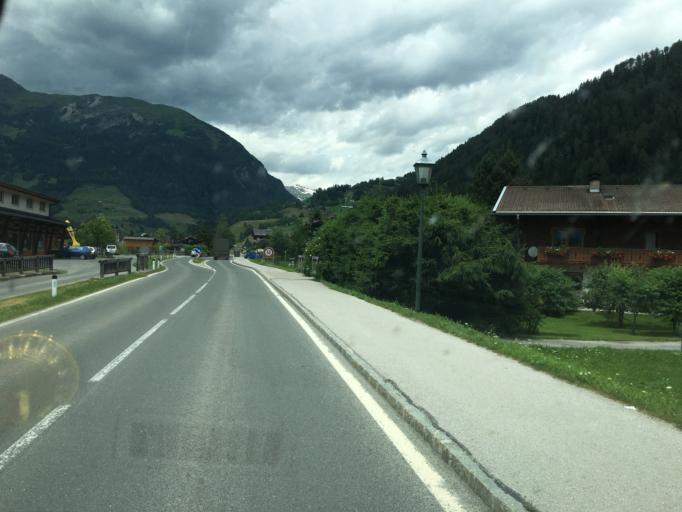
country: AT
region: Carinthia
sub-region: Politischer Bezirk Spittal an der Drau
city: Grosskirchheim
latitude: 46.9711
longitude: 12.8951
